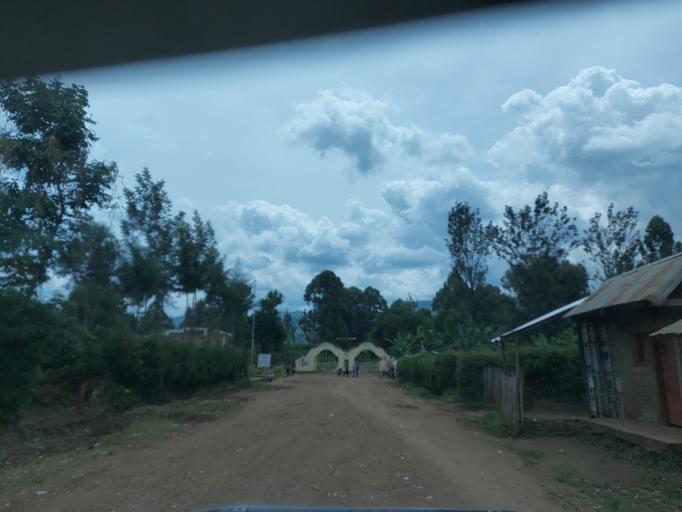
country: CD
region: South Kivu
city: Bukavu
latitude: -2.2441
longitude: 28.8145
